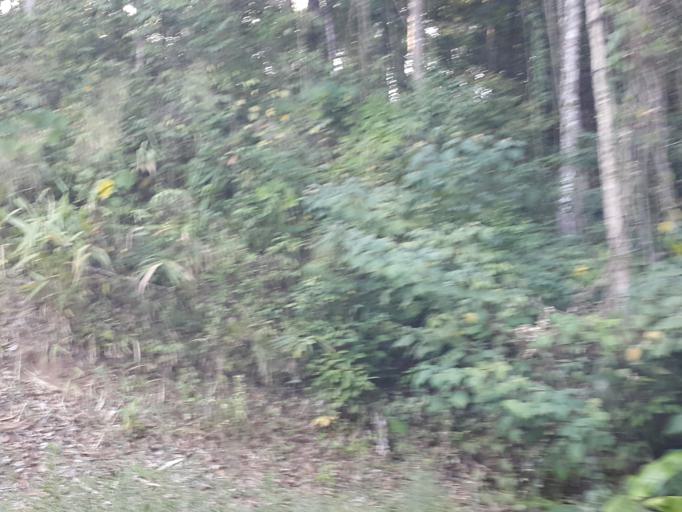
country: TH
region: Chiang Mai
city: Samoeng
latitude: 19.0238
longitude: 98.7630
